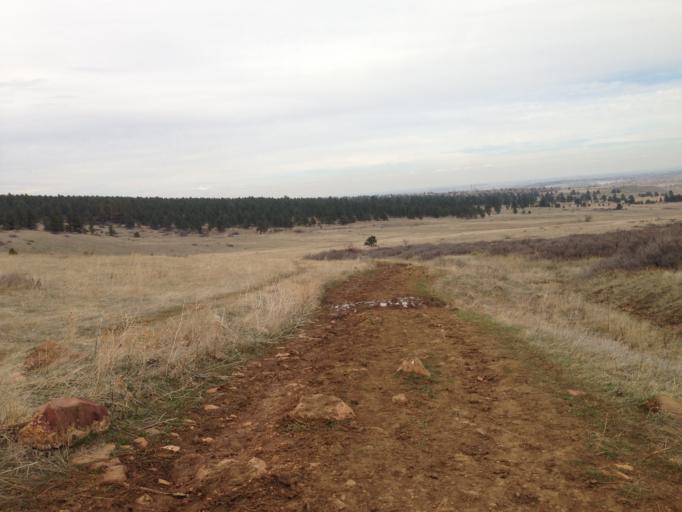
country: US
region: Colorado
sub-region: Boulder County
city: Boulder
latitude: 39.9508
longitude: -105.2664
